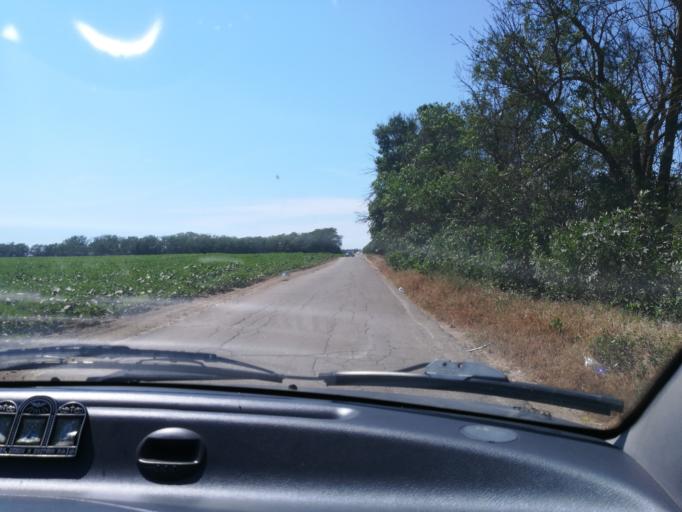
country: RU
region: Krasnodarskiy
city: Blagovetschenskaya
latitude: 45.0579
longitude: 37.1036
